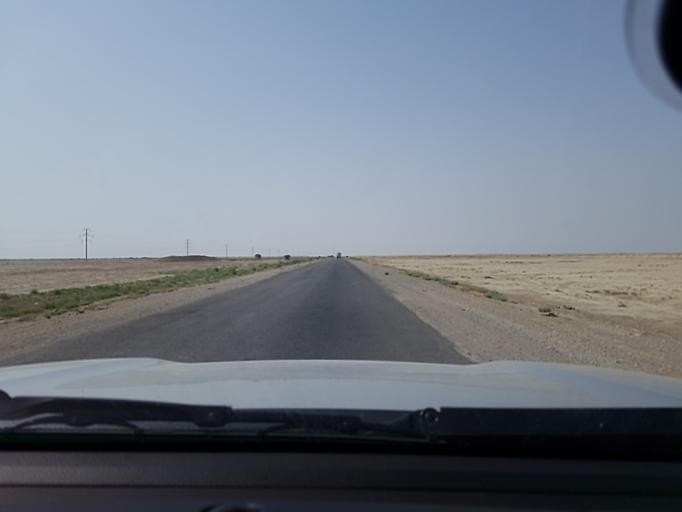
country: TM
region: Balkan
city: Gumdag
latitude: 38.8665
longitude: 54.5944
